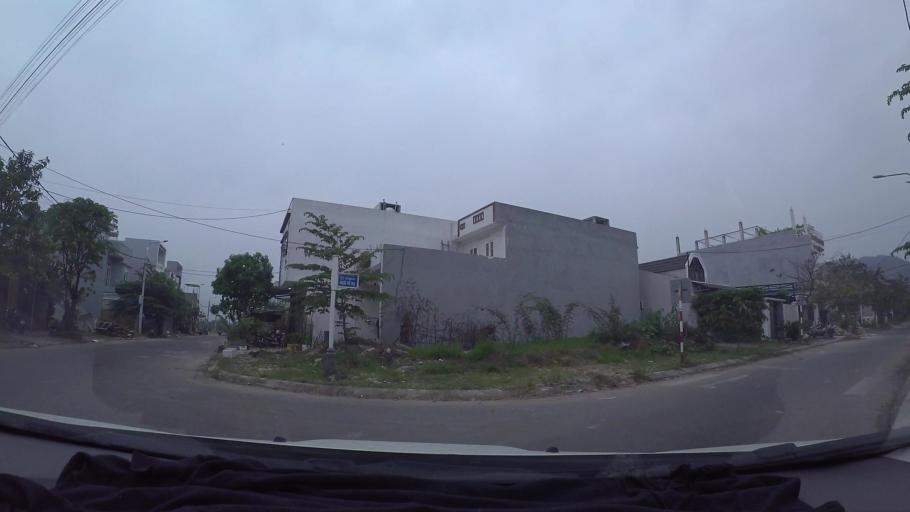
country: VN
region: Da Nang
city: Thanh Khe
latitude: 16.0440
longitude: 108.1789
